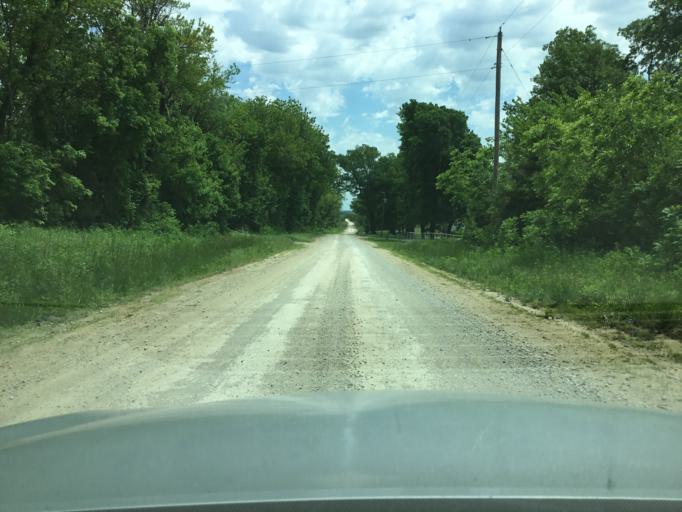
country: US
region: Kansas
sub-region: Montgomery County
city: Caney
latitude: 37.0952
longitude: -95.8109
